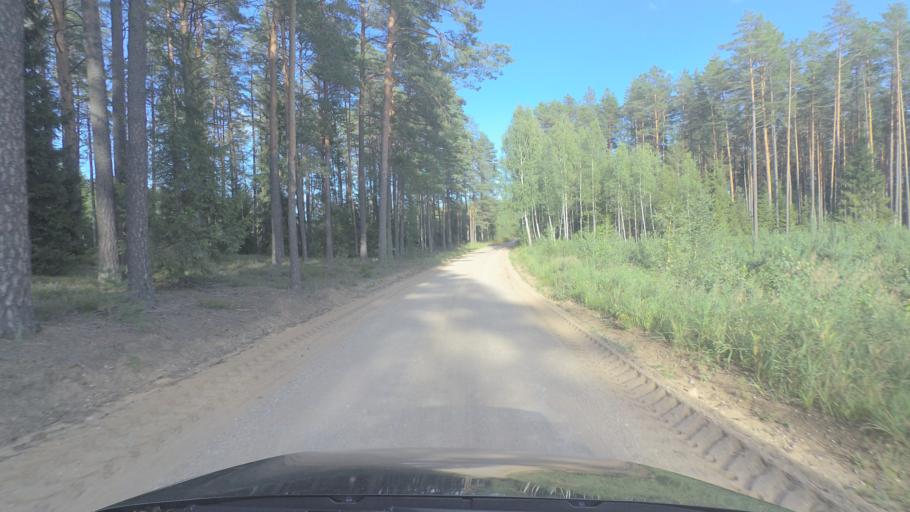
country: LT
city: Pabrade
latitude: 55.1620
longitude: 25.8172
